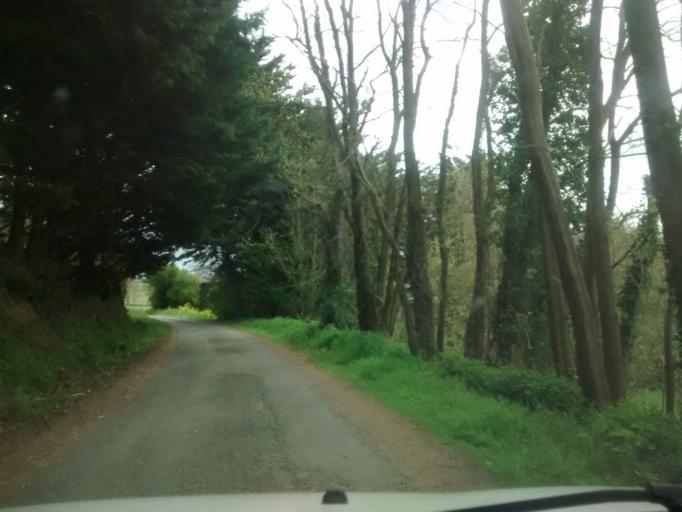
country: FR
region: Brittany
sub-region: Departement d'Ille-et-Vilaine
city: Saint-Jouan-des-Guerets
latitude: 48.5819
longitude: -1.9612
